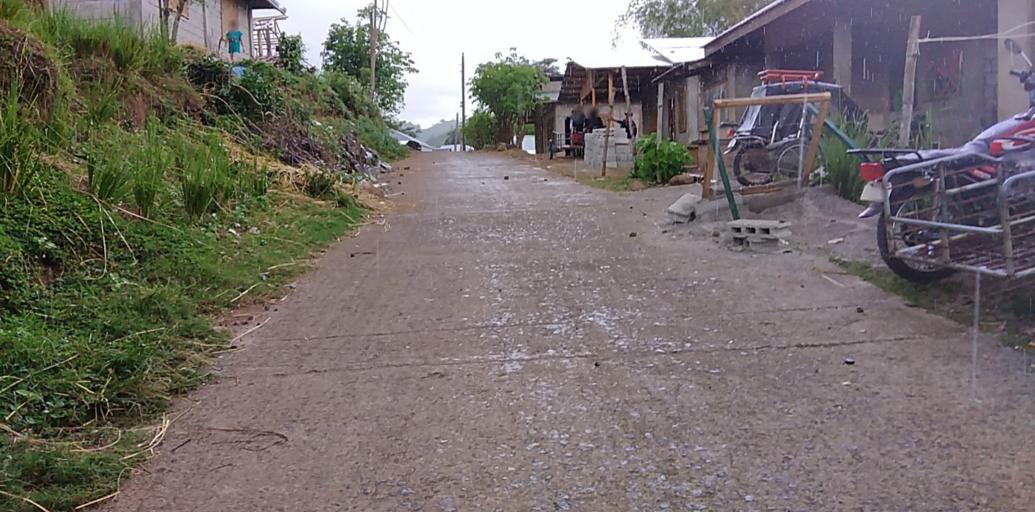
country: PH
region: Central Luzon
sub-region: Province of Pampanga
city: Babo-Pangulo
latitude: 15.1083
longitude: 120.4897
